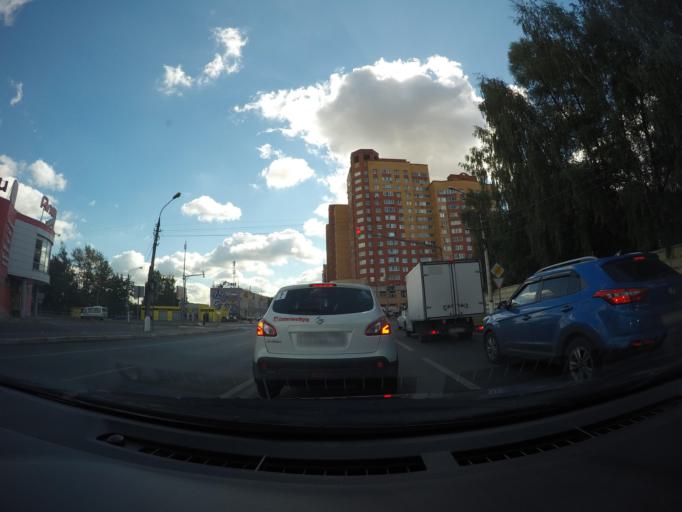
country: RU
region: Moskovskaya
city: Ramenskoye
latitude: 55.5823
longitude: 38.2433
